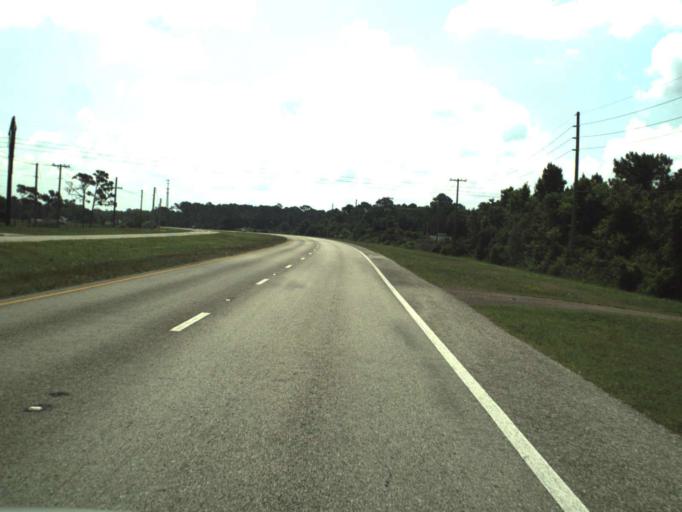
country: US
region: Florida
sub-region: Volusia County
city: Samsula-Spruce Creek
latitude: 29.0123
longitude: -81.0856
